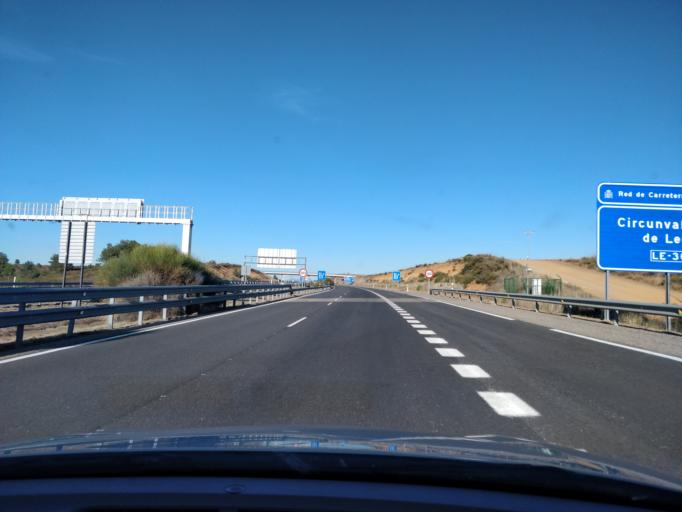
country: ES
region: Castille and Leon
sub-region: Provincia de Leon
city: San Andres del Rabanedo
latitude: 42.5716
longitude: -5.6367
